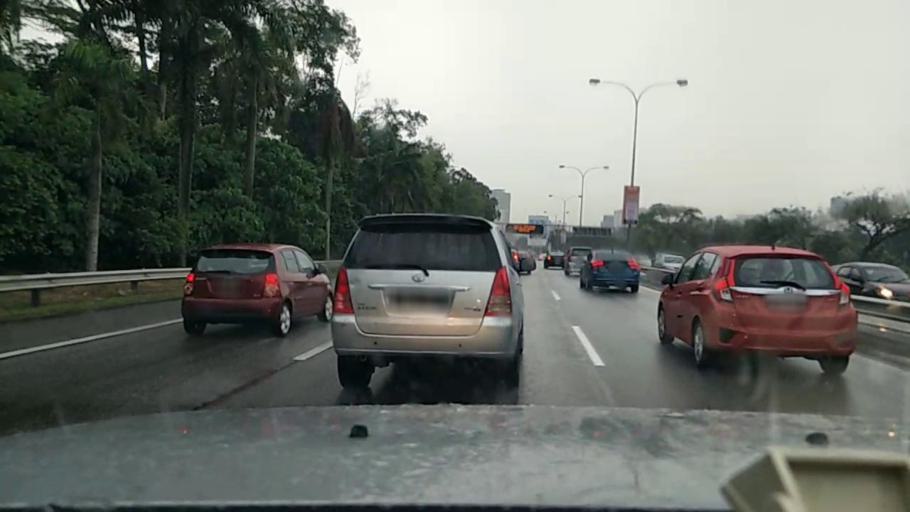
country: MY
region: Kuala Lumpur
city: Kuala Lumpur
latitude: 3.1095
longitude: 101.6905
